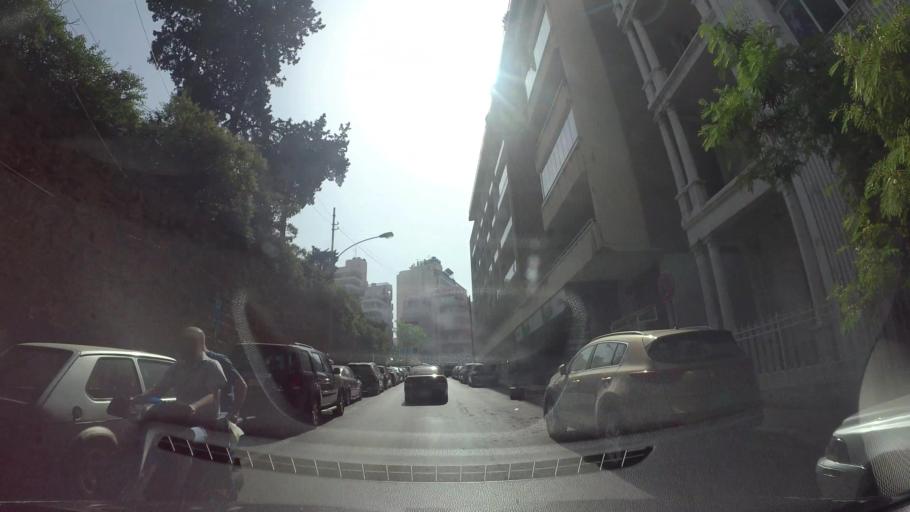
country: LB
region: Beyrouth
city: Ra's Bayrut
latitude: 33.8996
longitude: 35.4886
